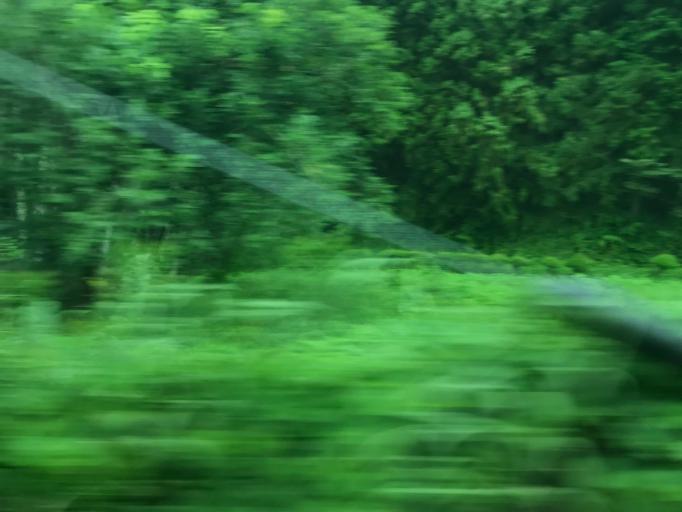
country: JP
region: Fukushima
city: Ishikawa
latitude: 37.1281
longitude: 140.2441
